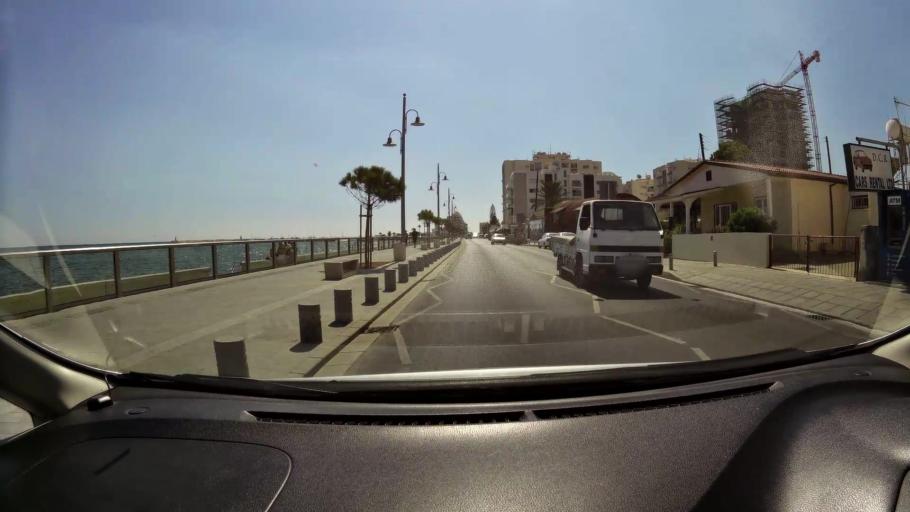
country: CY
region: Larnaka
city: Larnaca
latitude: 34.9026
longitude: 33.6377
